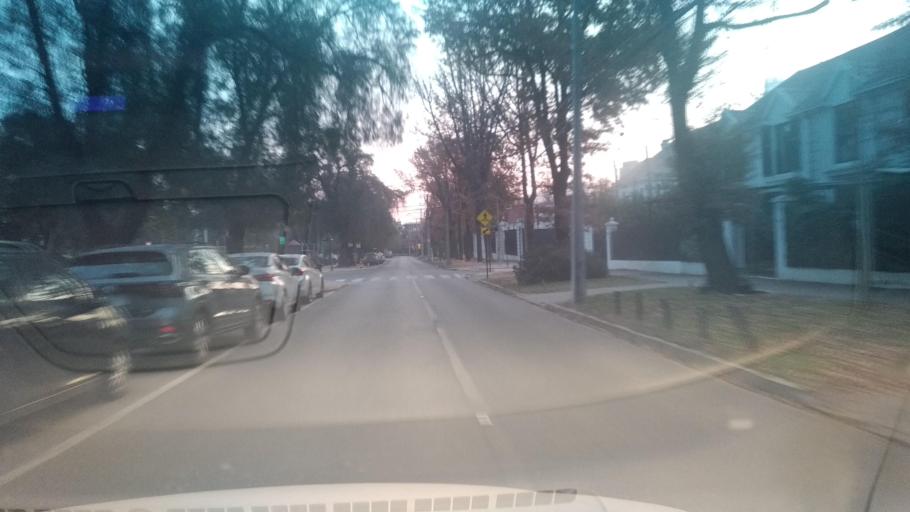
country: CL
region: Santiago Metropolitan
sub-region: Provincia de Santiago
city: Villa Presidente Frei, Nunoa, Santiago, Chile
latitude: -33.4206
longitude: -70.5909
